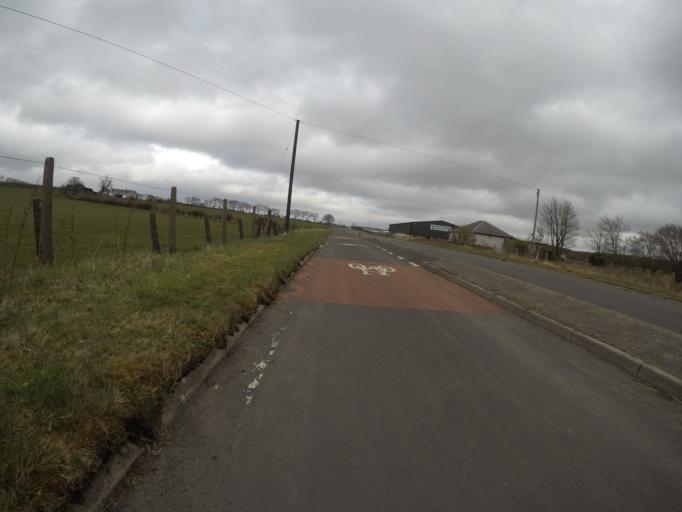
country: GB
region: Scotland
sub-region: East Ayrshire
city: Stewarton
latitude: 55.6741
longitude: -4.4369
